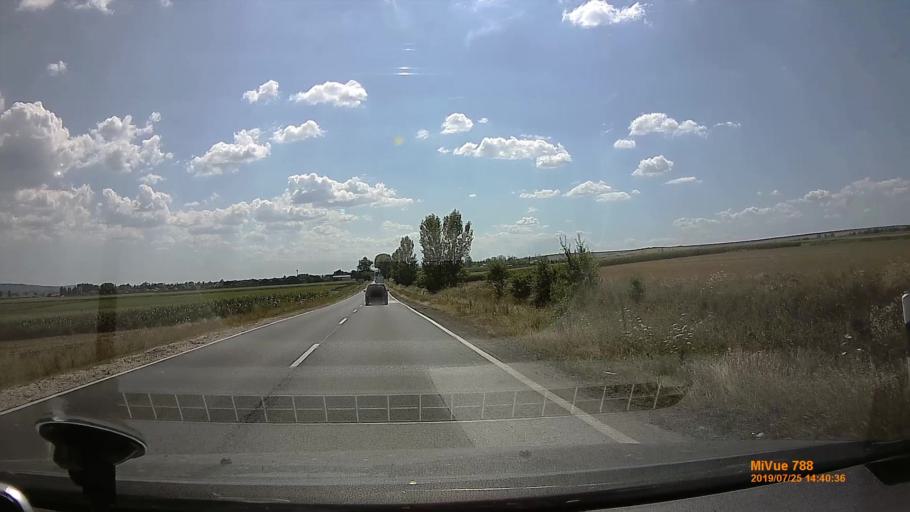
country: HU
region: Borsod-Abauj-Zemplen
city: Halmaj
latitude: 48.2895
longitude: 21.0387
